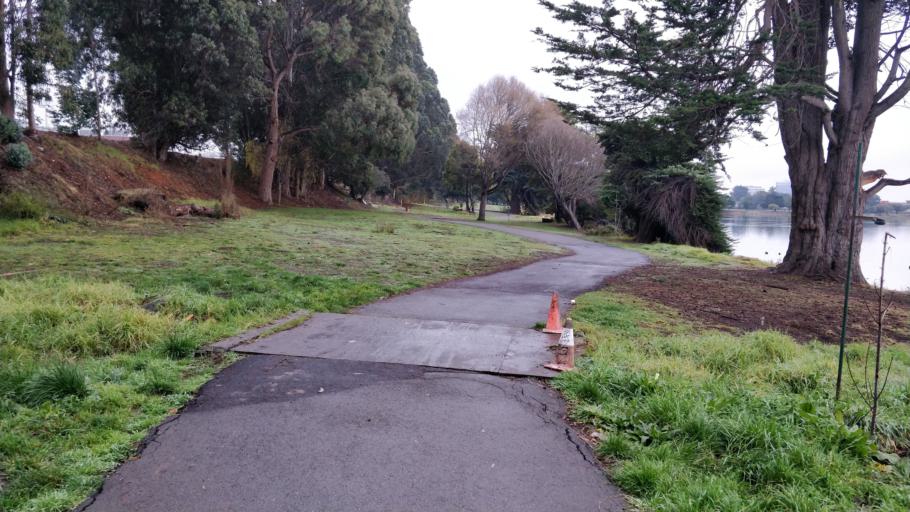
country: US
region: California
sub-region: Alameda County
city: Emeryville
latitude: 37.8552
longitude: -122.2974
